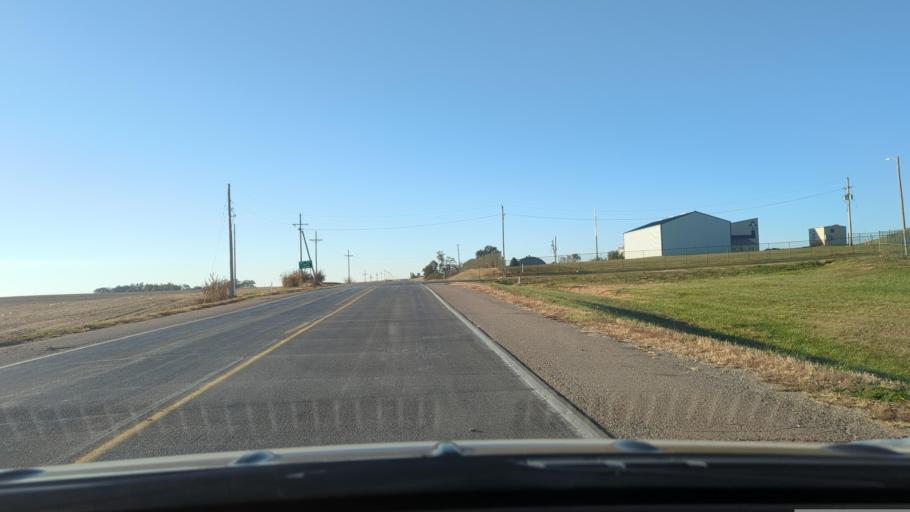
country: US
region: Nebraska
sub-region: Sarpy County
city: Springfield
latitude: 41.0999
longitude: -96.1577
